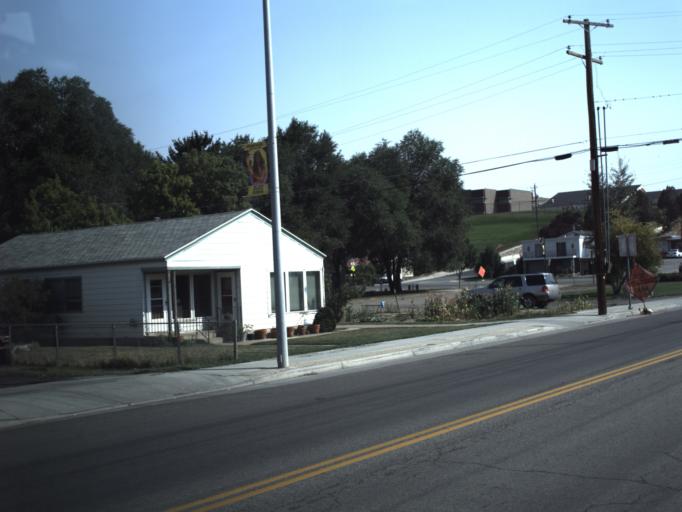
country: US
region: Utah
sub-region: Summit County
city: Coalville
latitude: 40.9137
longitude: -111.3983
